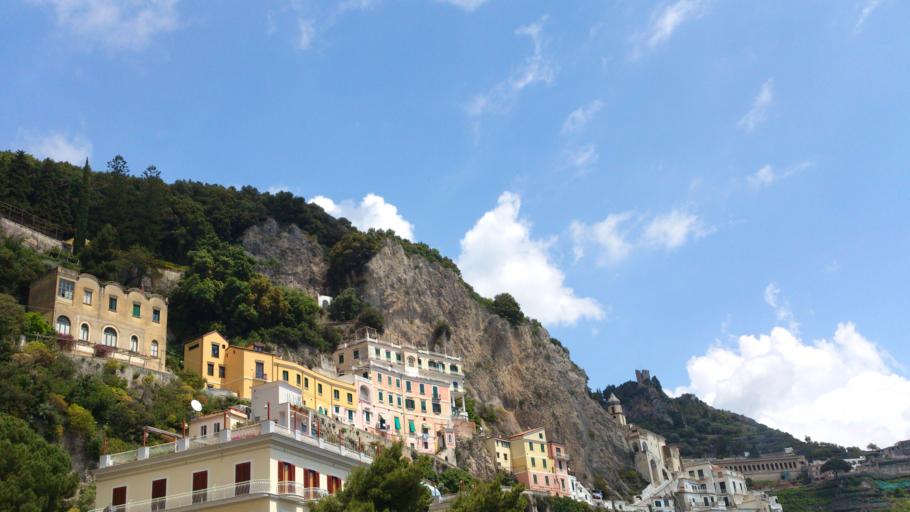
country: IT
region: Campania
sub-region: Provincia di Salerno
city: Amalfi
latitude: 40.6326
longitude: 14.5980
